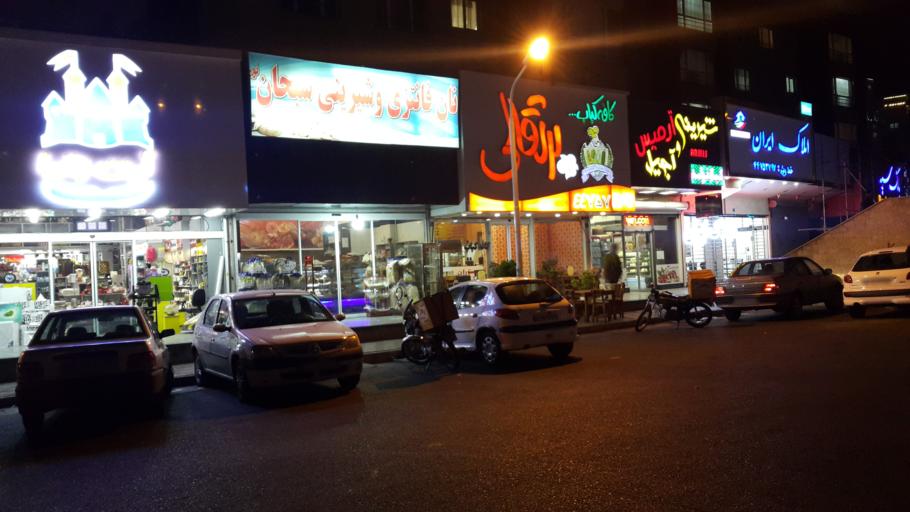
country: IR
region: Tehran
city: Shahr-e Qods
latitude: 35.7538
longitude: 51.2180
